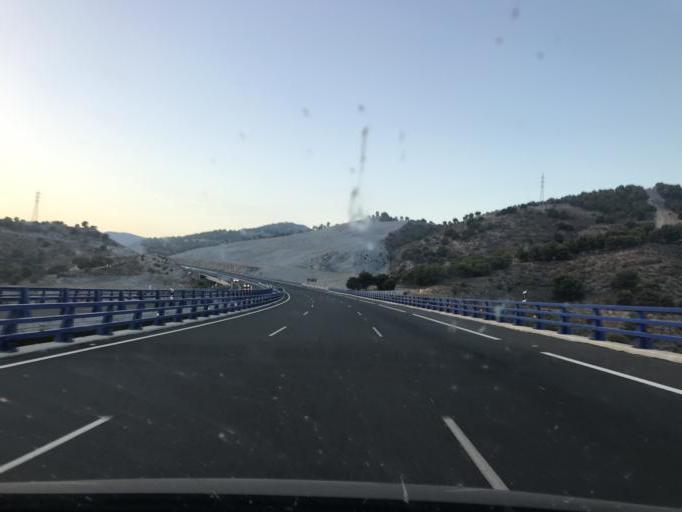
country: ES
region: Andalusia
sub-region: Provincia de Granada
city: Motril
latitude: 36.7692
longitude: -3.4859
